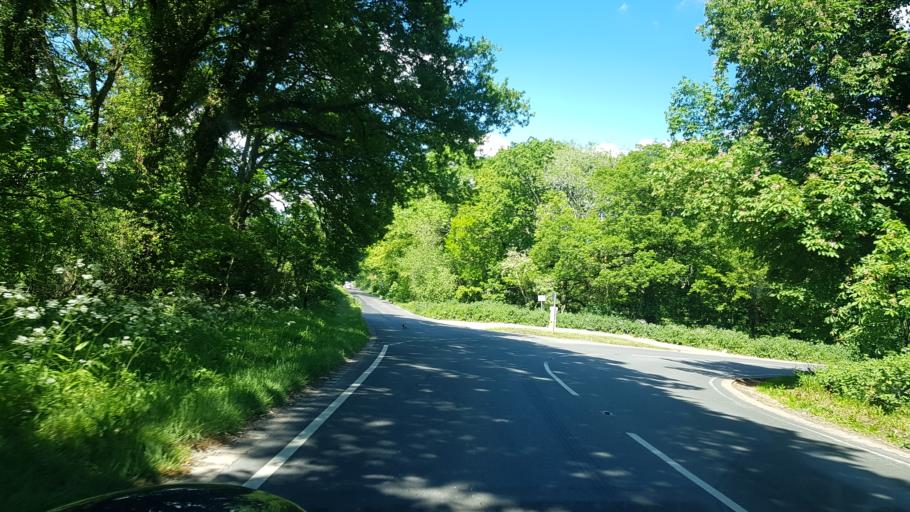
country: GB
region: England
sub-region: Surrey
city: Cranleigh
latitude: 51.1369
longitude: -0.5327
